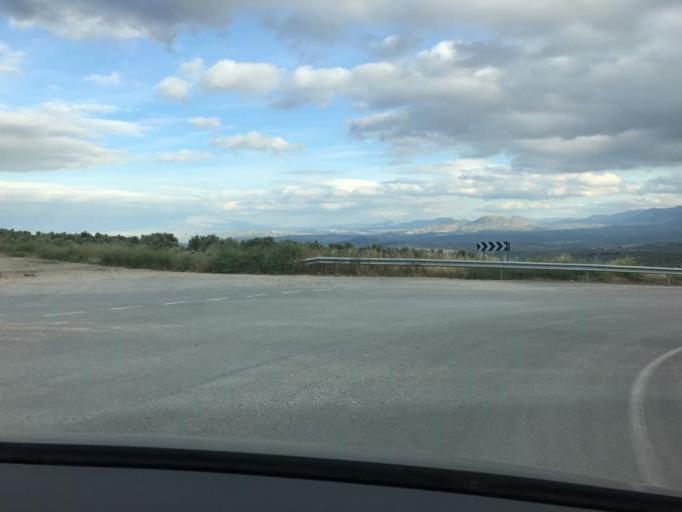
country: ES
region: Andalusia
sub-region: Provincia de Jaen
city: Ubeda
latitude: 37.9977
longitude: -3.3812
